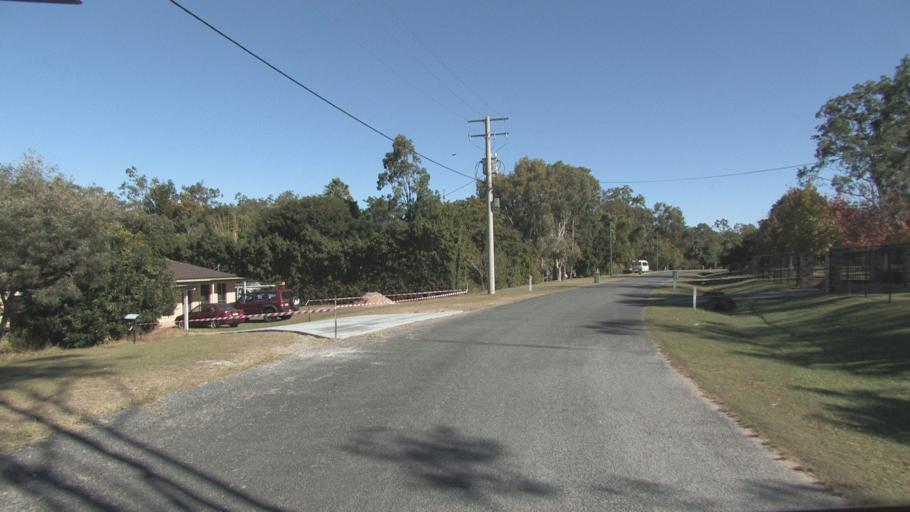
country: AU
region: Queensland
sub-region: Logan
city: Park Ridge South
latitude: -27.7339
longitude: 153.0413
